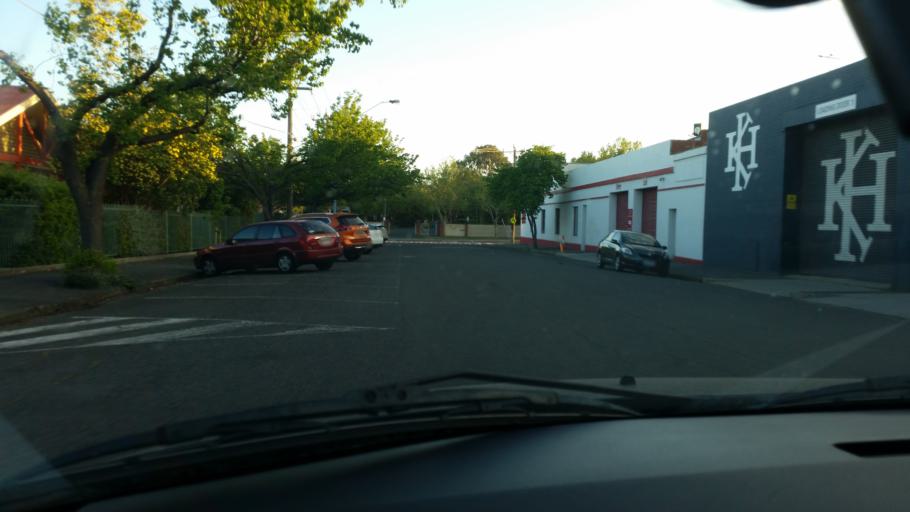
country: AU
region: Victoria
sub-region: Moonee Valley
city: Flemington
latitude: -37.7870
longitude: 144.9268
